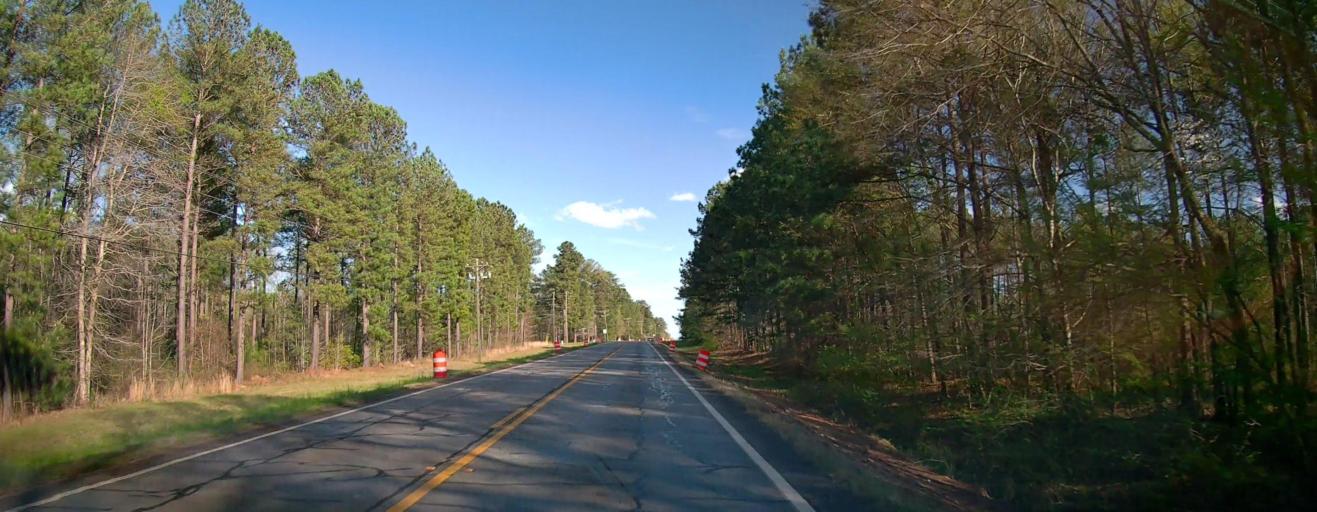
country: US
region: Georgia
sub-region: Putnam County
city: Eatonton
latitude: 33.1722
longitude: -83.3933
